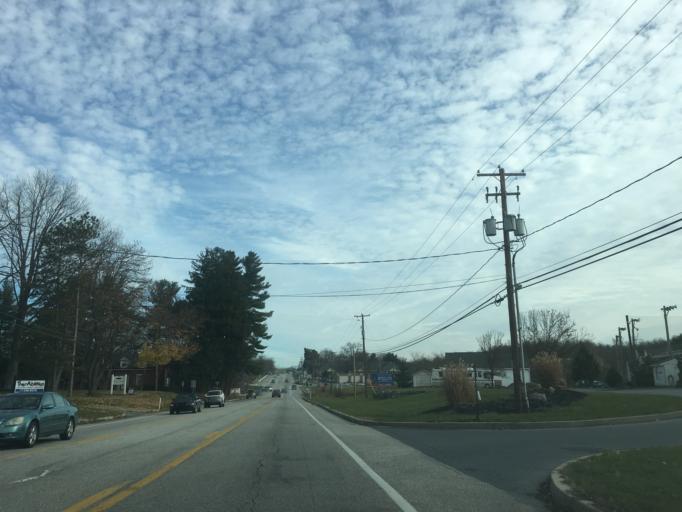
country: US
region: Pennsylvania
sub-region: Dauphin County
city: Lawrence Park
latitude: 40.3357
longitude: -76.8295
